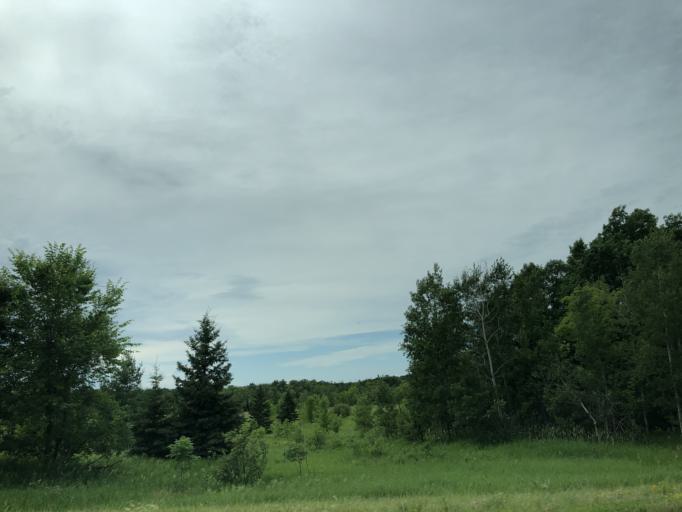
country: US
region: Minnesota
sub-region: Stearns County
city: Collegeville
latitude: 45.5815
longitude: -94.3578
